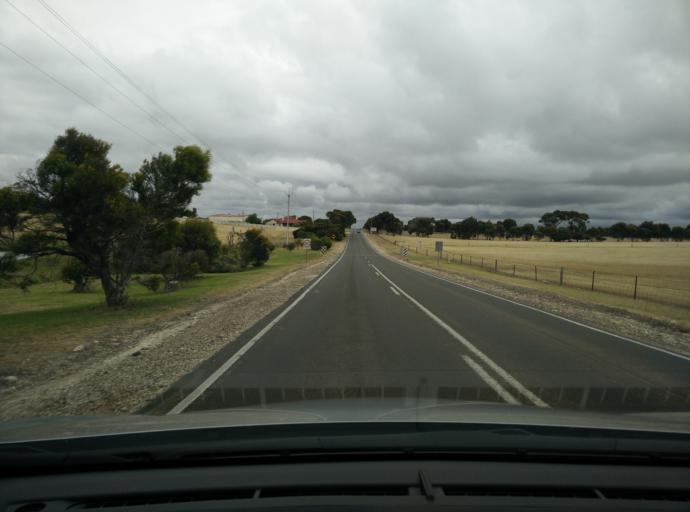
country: AU
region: South Australia
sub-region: Kangaroo Island
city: Kingscote
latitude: -35.6528
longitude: 137.6265
